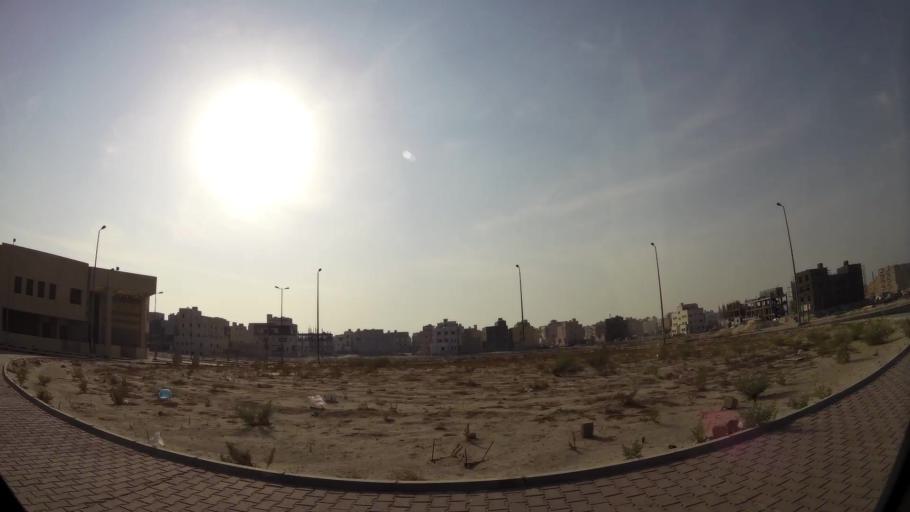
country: KW
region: Mubarak al Kabir
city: Mubarak al Kabir
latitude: 29.1997
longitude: 48.1012
